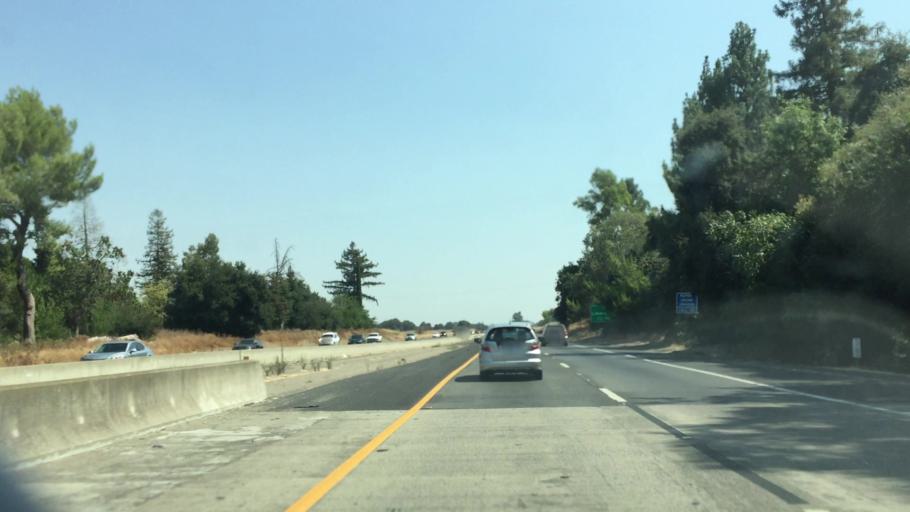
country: US
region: California
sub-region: Sacramento County
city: Galt
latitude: 38.2420
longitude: -121.2858
